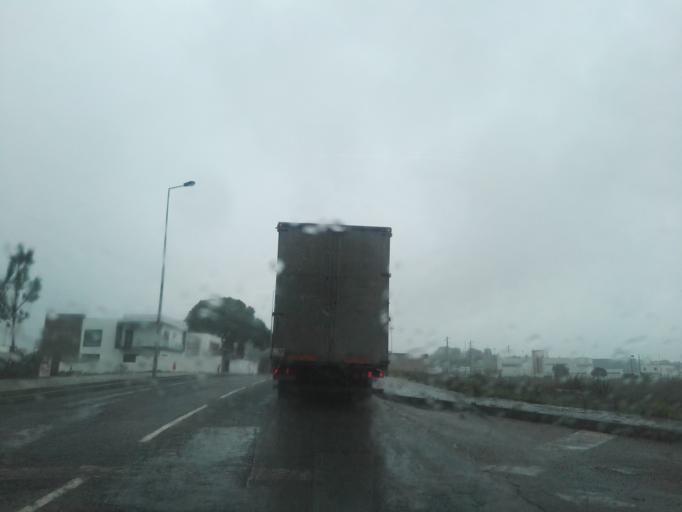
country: PT
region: Santarem
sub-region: Cartaxo
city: Cartaxo
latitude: 39.1614
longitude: -8.7981
